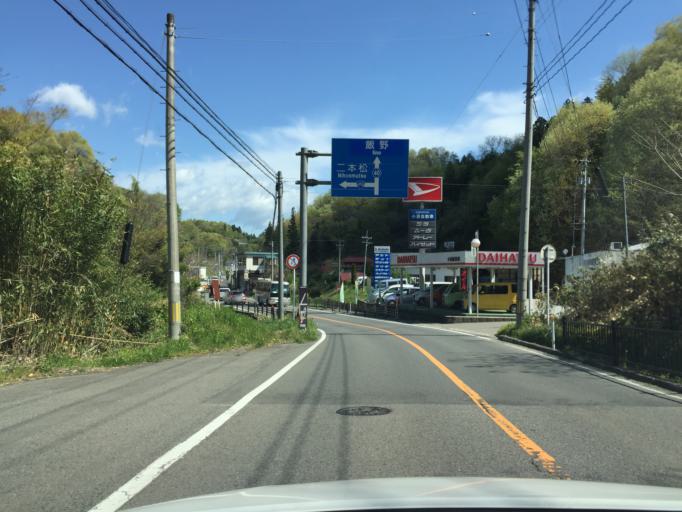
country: JP
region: Fukushima
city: Nihommatsu
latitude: 37.5671
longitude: 140.5090
